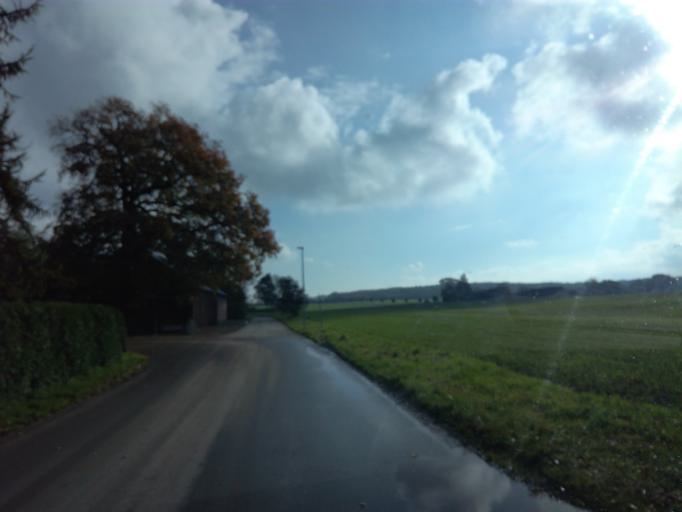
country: DK
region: South Denmark
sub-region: Vejle Kommune
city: Borkop
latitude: 55.6403
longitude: 9.6113
